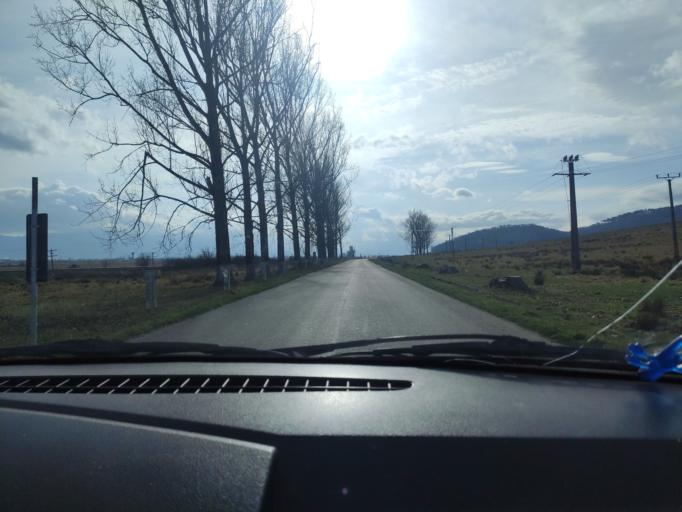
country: RO
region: Brasov
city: Codlea
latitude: 45.7306
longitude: 25.4575
